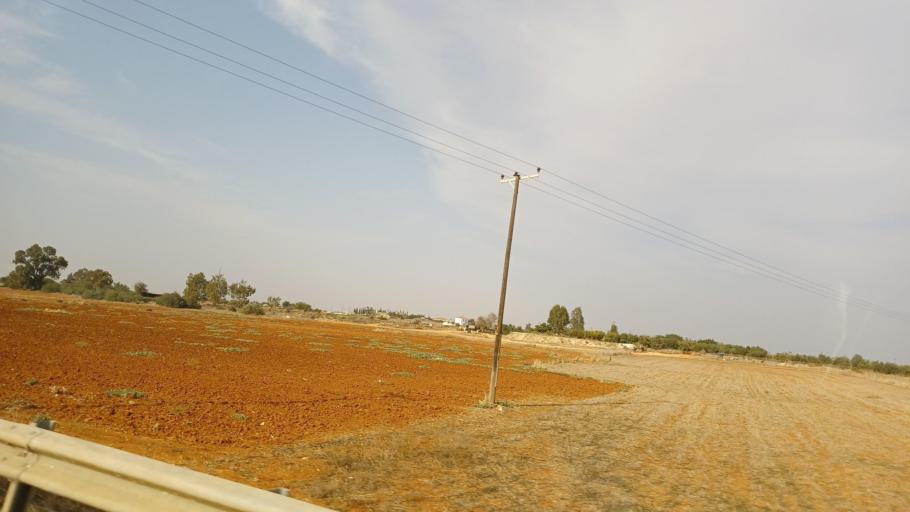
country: CY
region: Ammochostos
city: Frenaros
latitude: 35.0481
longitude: 33.9138
